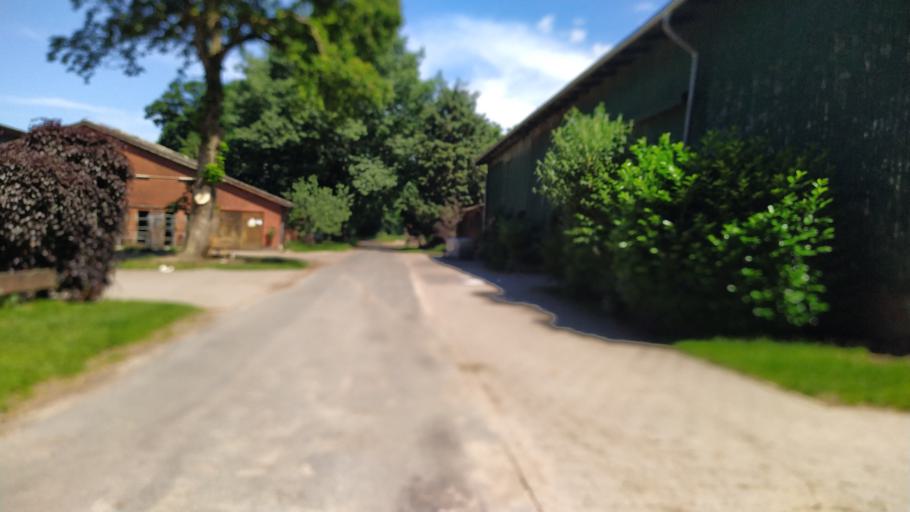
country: DE
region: Lower Saxony
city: Bargstedt
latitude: 53.4950
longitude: 9.4360
